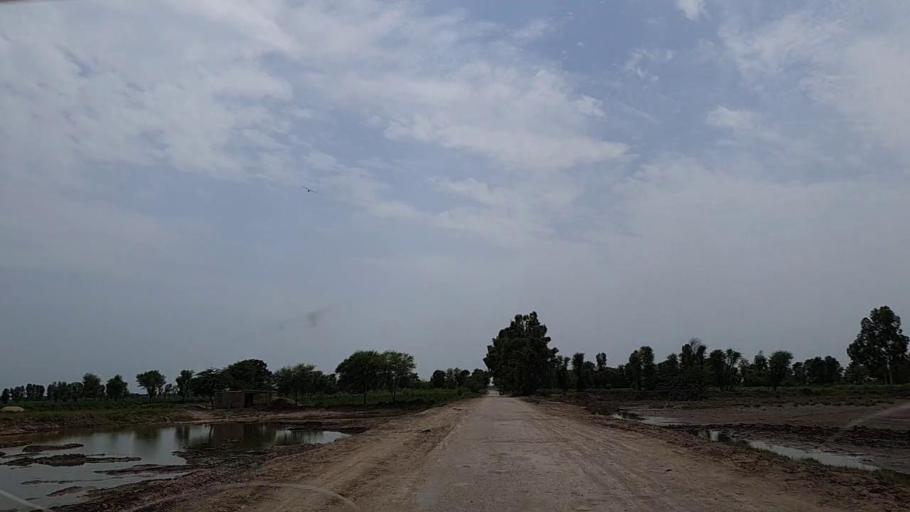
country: PK
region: Sindh
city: Tharu Shah
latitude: 26.9235
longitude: 68.1020
